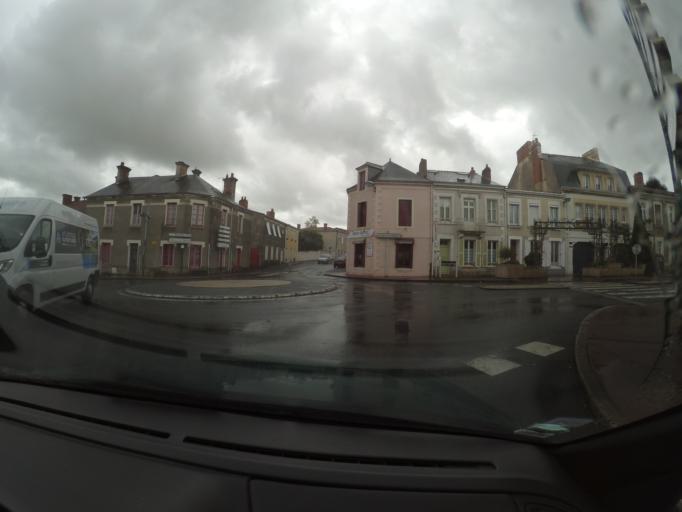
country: FR
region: Pays de la Loire
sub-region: Departement de la Loire-Atlantique
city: Vallet
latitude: 47.1610
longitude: -1.2688
